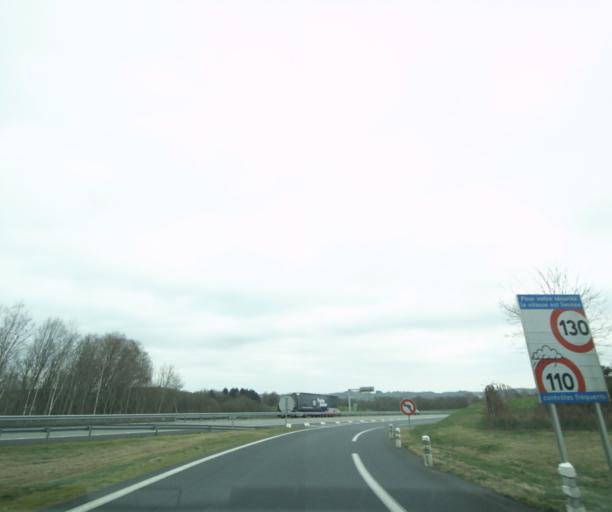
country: FR
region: Limousin
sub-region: Departement de la Correze
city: Vigeois
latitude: 45.3582
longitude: 1.5694
